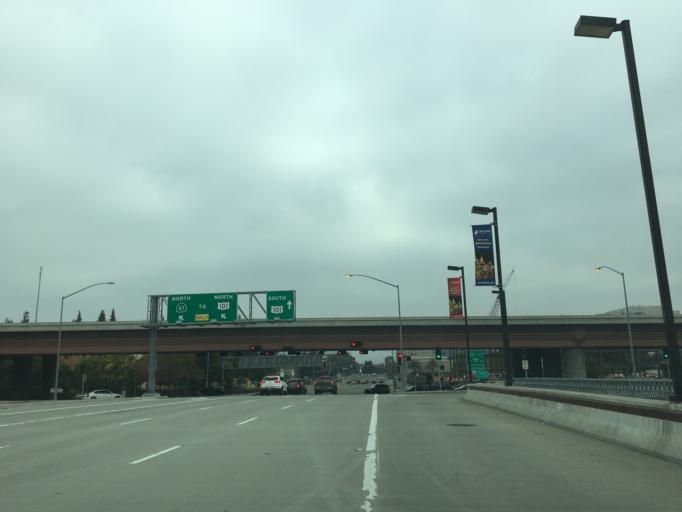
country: US
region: California
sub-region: Santa Clara County
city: San Jose
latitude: 37.3639
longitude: -121.9197
